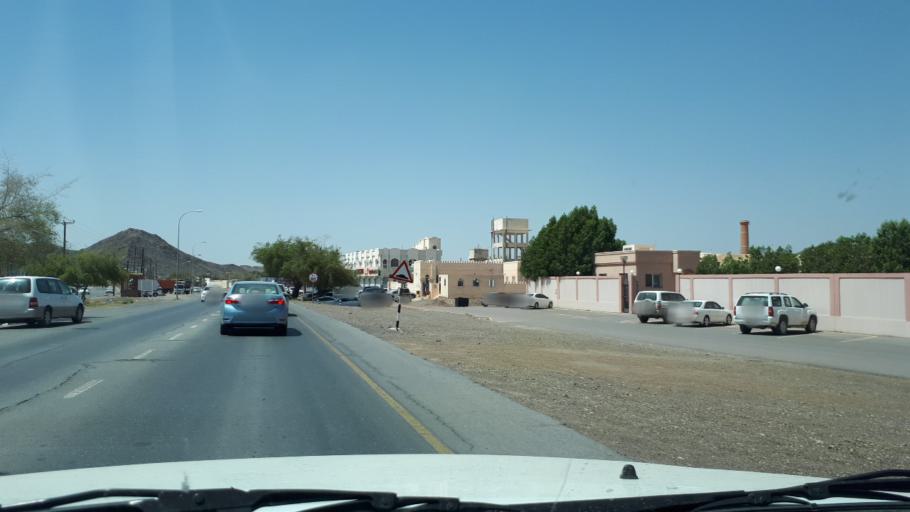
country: OM
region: Muhafazat ad Dakhiliyah
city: Bahla'
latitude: 22.9872
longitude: 57.3099
